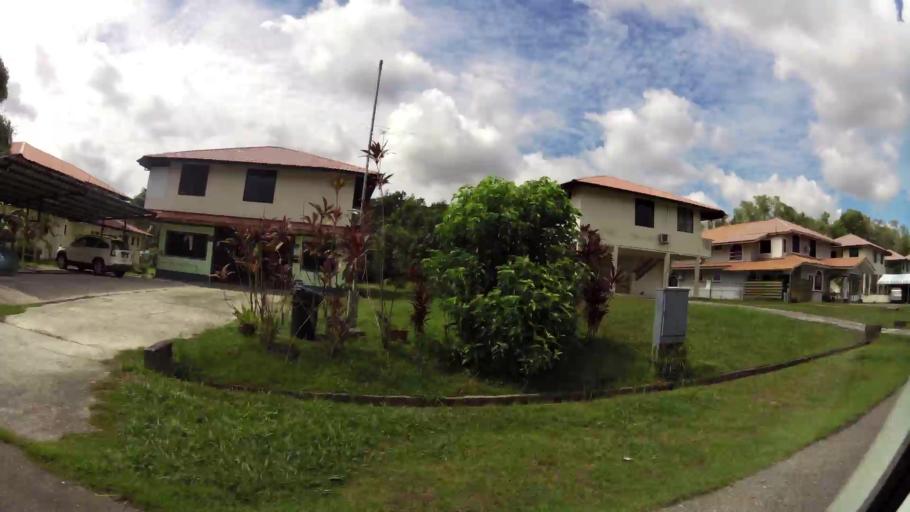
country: BN
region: Brunei and Muara
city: Bandar Seri Begawan
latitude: 4.9329
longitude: 114.9026
